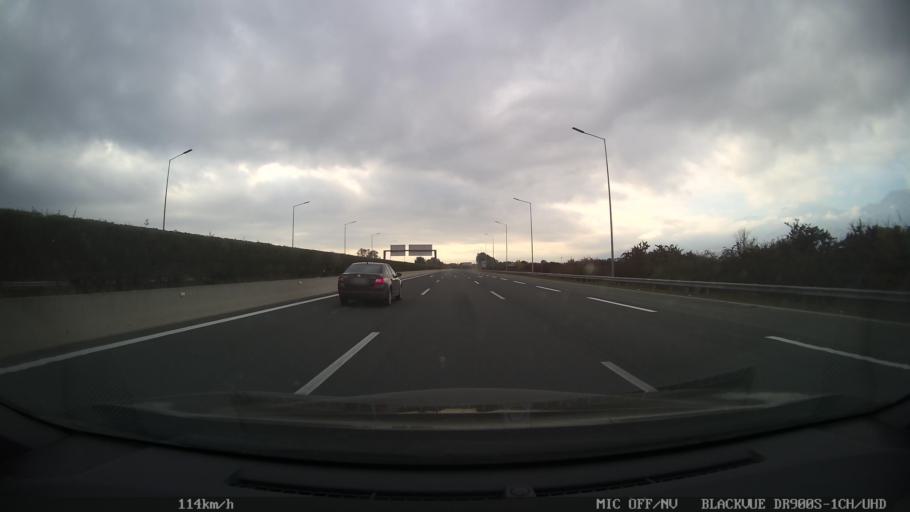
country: GR
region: Central Macedonia
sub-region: Nomos Pierias
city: Nea Efesos
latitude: 40.1913
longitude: 22.5497
